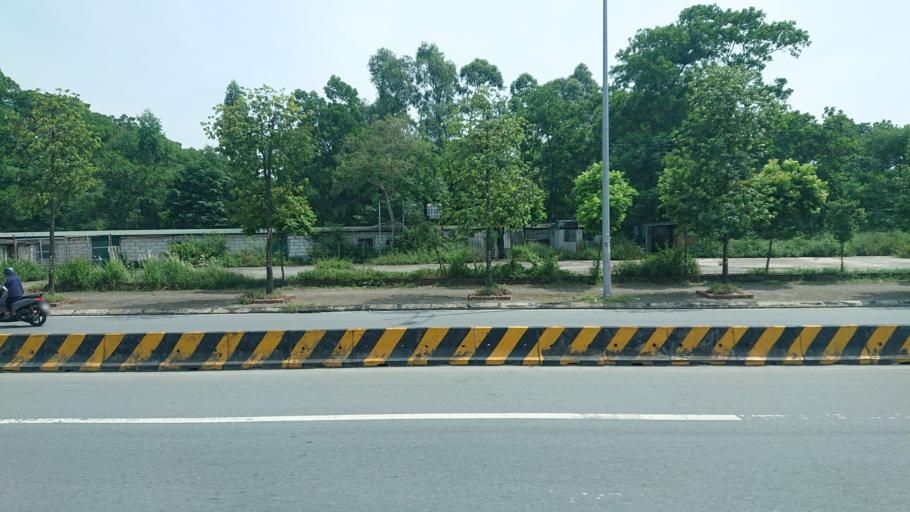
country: VN
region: Ha Noi
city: Soc Son
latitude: 21.2078
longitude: 105.8213
